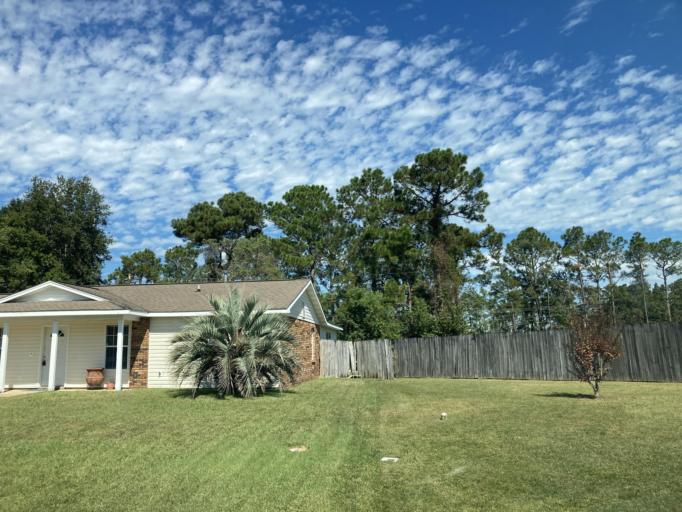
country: US
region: Mississippi
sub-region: Jackson County
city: Saint Martin
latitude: 30.4529
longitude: -88.8636
